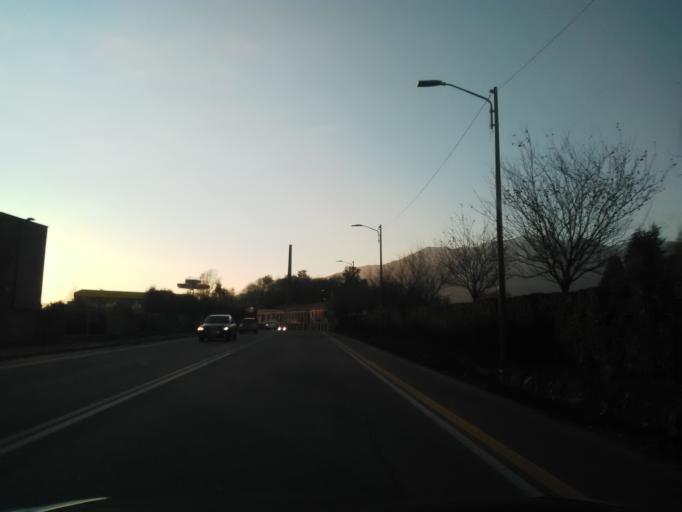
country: IT
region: Piedmont
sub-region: Provincia di Biella
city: Occhieppo Inferiore
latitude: 45.5570
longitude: 8.0329
